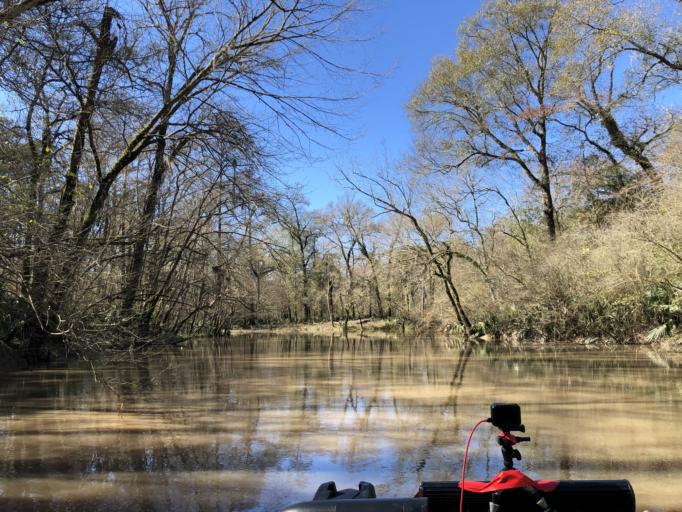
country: US
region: Louisiana
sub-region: Calcasieu Parish
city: Iowa
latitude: 30.3081
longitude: -93.0686
